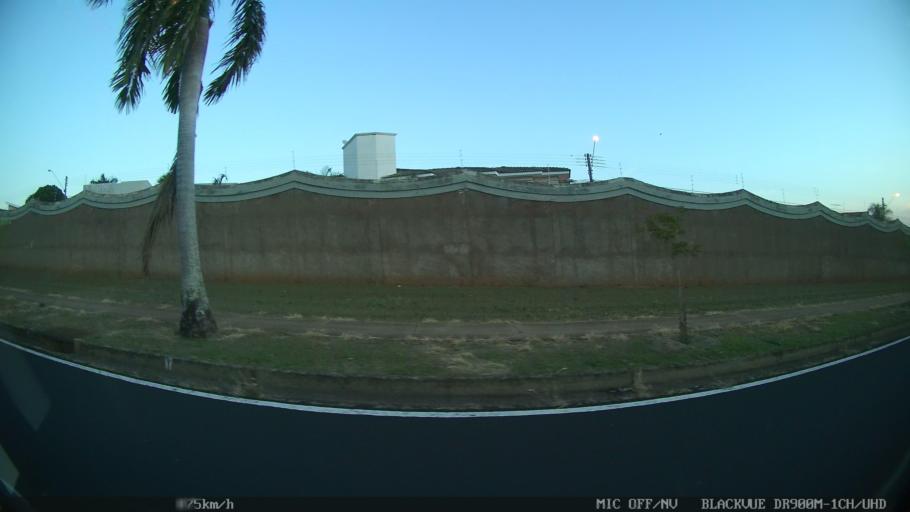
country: BR
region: Sao Paulo
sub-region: Sao Jose Do Rio Preto
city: Sao Jose do Rio Preto
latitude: -20.8169
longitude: -49.3416
